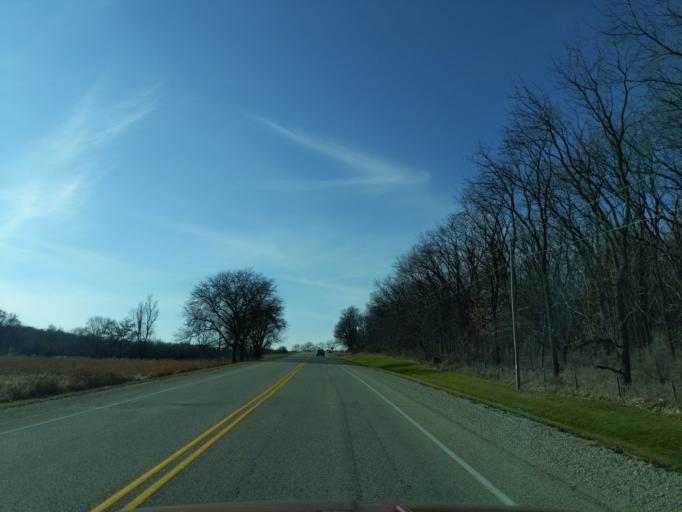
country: US
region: Wisconsin
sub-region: Rock County
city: Milton
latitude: 42.8233
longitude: -88.9483
